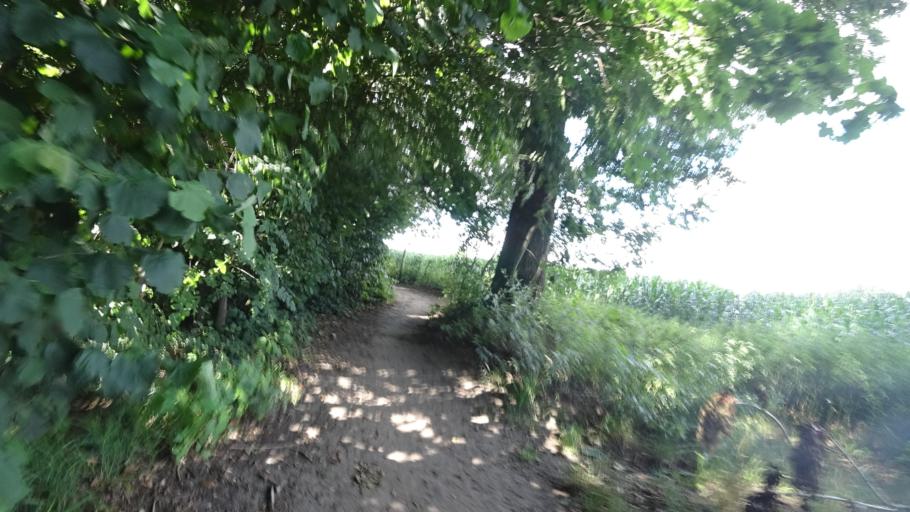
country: DE
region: North Rhine-Westphalia
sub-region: Regierungsbezirk Detmold
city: Guetersloh
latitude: 51.9416
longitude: 8.3995
